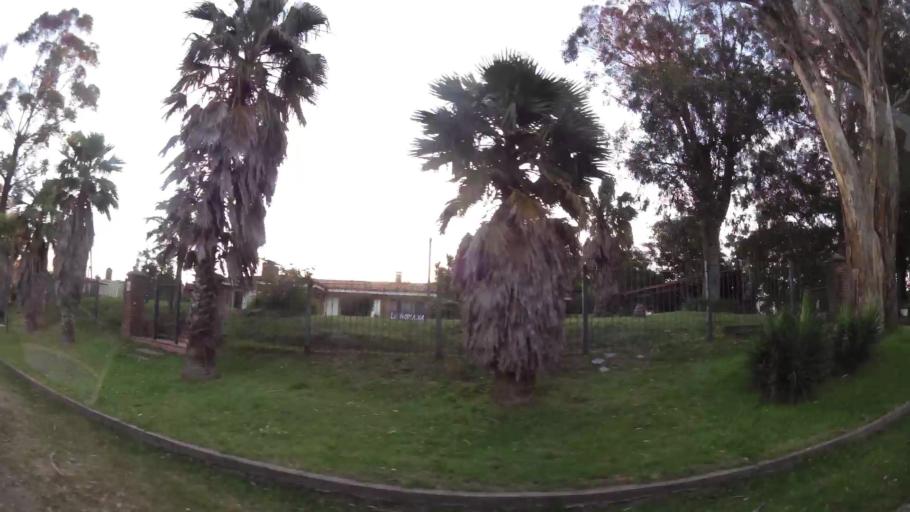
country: UY
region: Canelones
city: Atlantida
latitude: -34.7703
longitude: -55.7699
